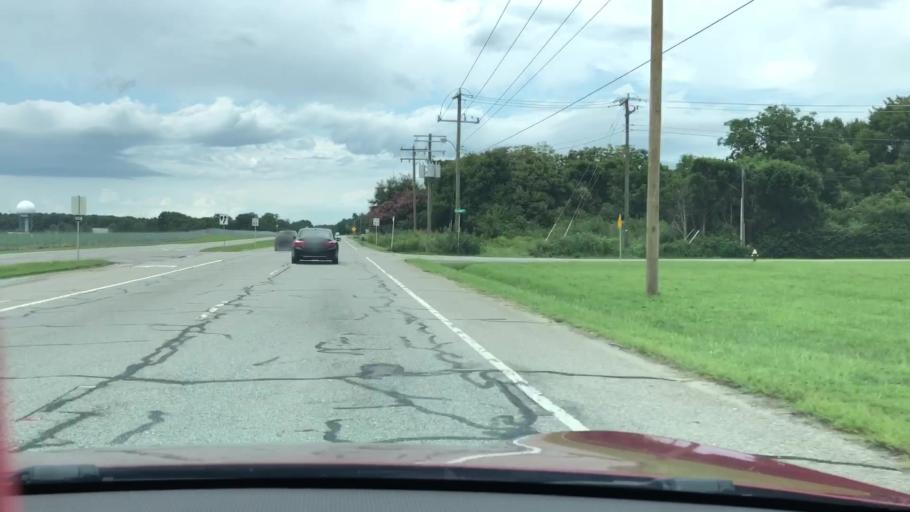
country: US
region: Virginia
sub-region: City of Virginia Beach
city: Virginia Beach
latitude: 36.8199
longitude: -76.0079
